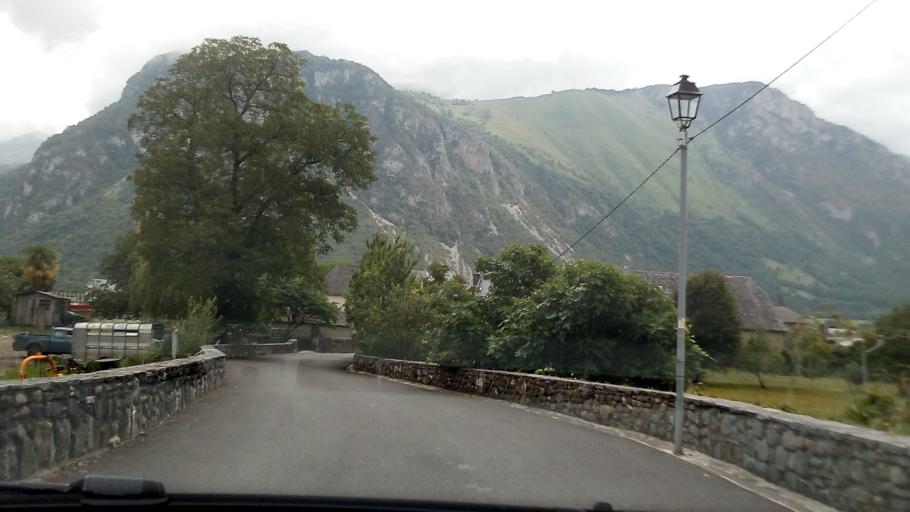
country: FR
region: Aquitaine
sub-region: Departement des Pyrenees-Atlantiques
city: Louvie-Juzon
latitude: 43.0566
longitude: -0.4380
